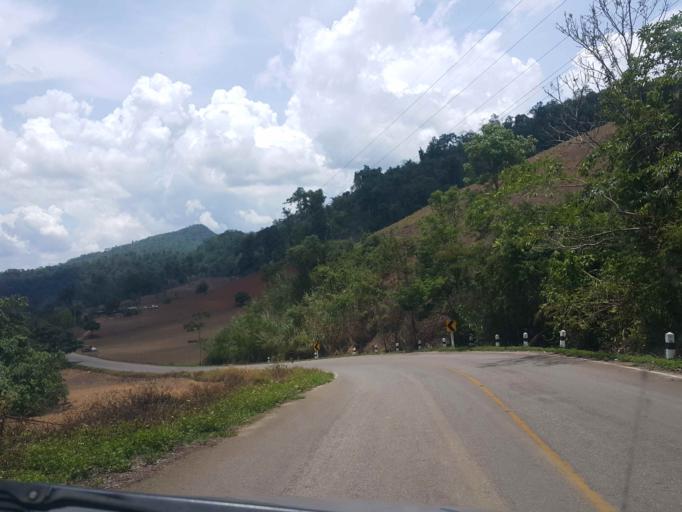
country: TH
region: Phayao
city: Chiang Muan
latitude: 18.9079
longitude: 100.1186
